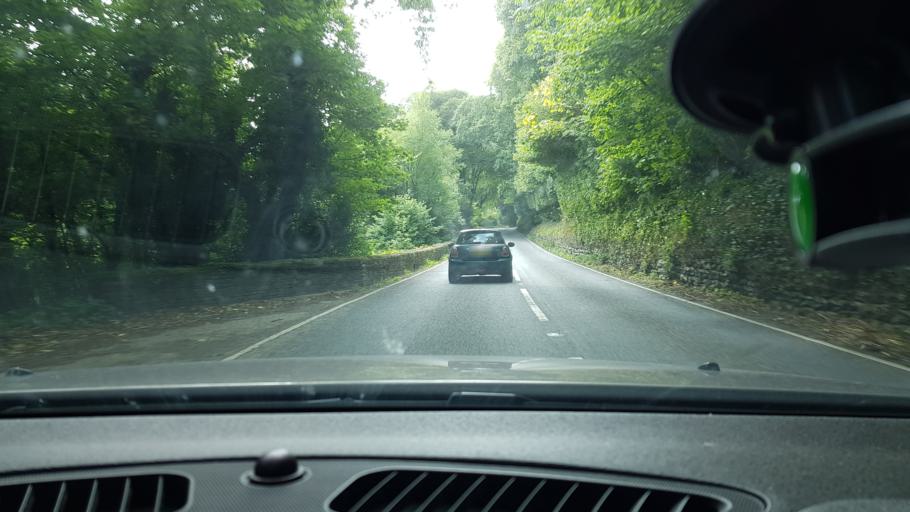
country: GB
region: England
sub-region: Cornwall
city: Helland
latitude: 50.5661
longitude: -4.7522
